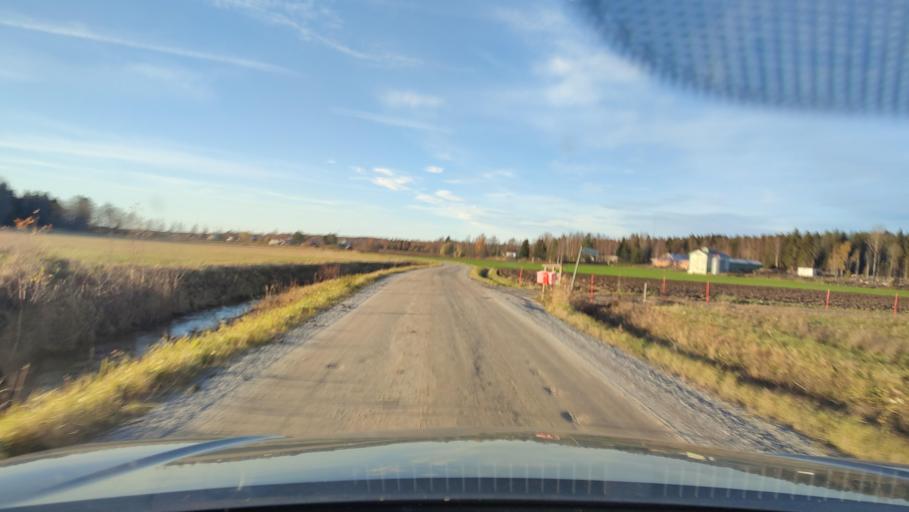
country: FI
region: Ostrobothnia
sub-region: Vaasa
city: Ristinummi
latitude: 63.0082
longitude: 21.7154
